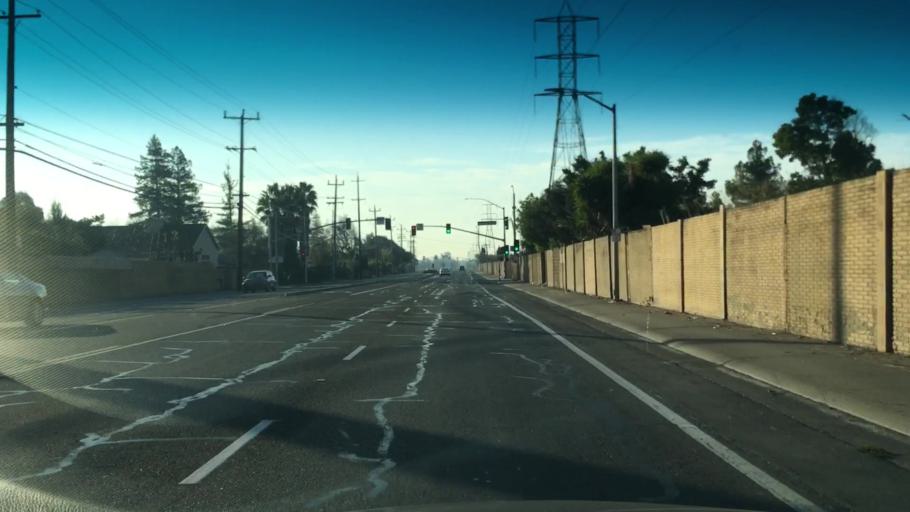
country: US
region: California
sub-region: Sacramento County
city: Florin
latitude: 38.4785
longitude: -121.4089
